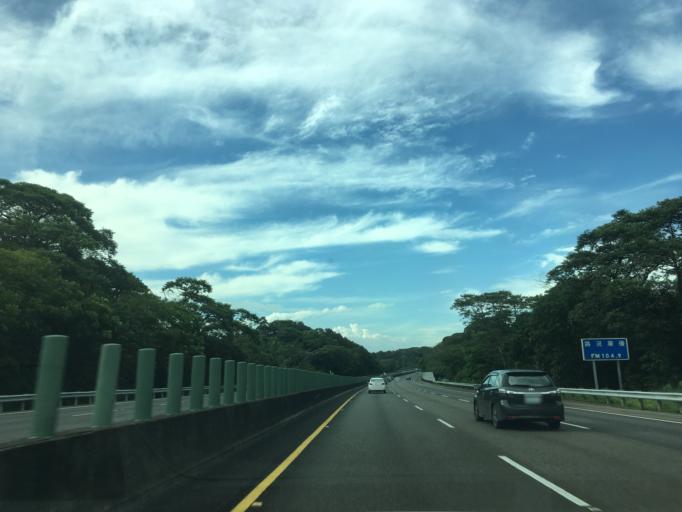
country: TW
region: Taiwan
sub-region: Chiayi
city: Jiayi Shi
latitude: 23.5682
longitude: 120.5053
